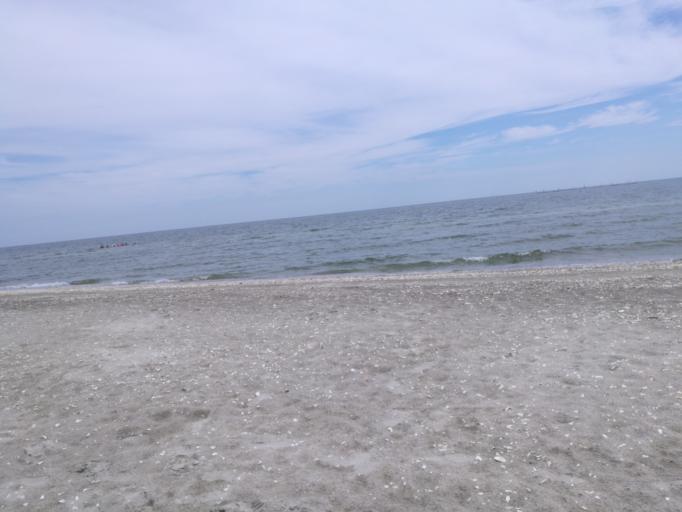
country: RO
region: Constanta
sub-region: Comuna Corbu
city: Corbu
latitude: 44.4258
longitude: 28.7626
